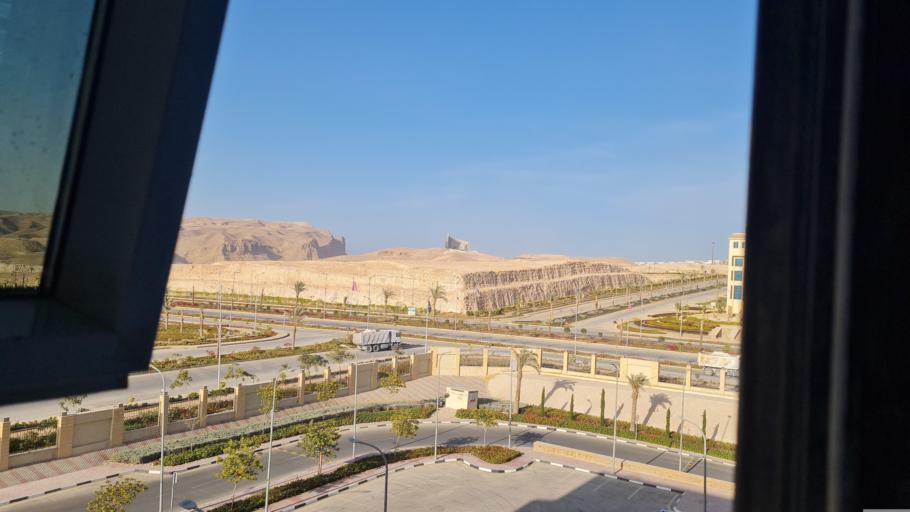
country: EG
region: As Suways
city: Ain Sukhna
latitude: 29.4331
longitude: 32.3981
